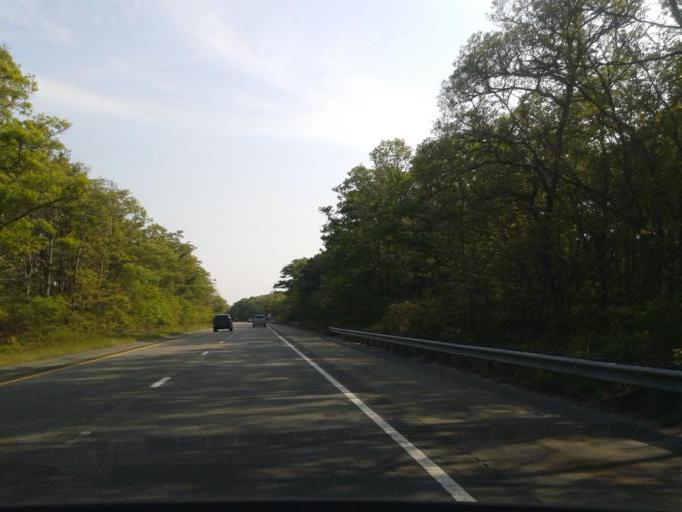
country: US
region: Massachusetts
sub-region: Barnstable County
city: West Falmouth
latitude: 41.6112
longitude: -70.6237
